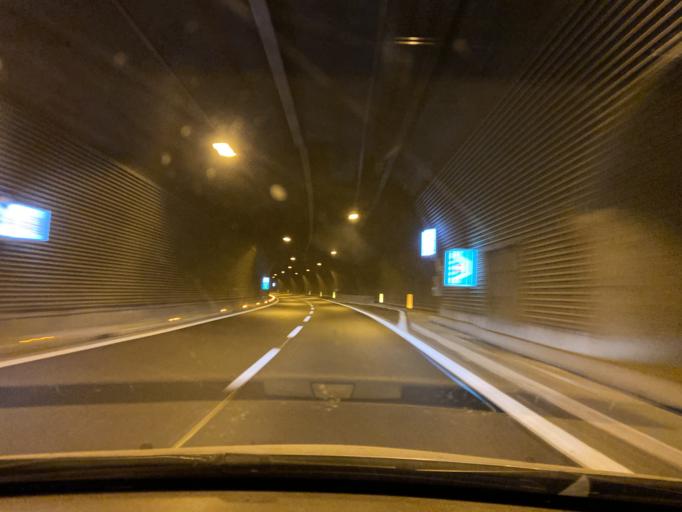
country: IT
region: Piedmont
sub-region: Provincia di Torino
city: Susa
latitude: 45.1408
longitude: 7.0682
